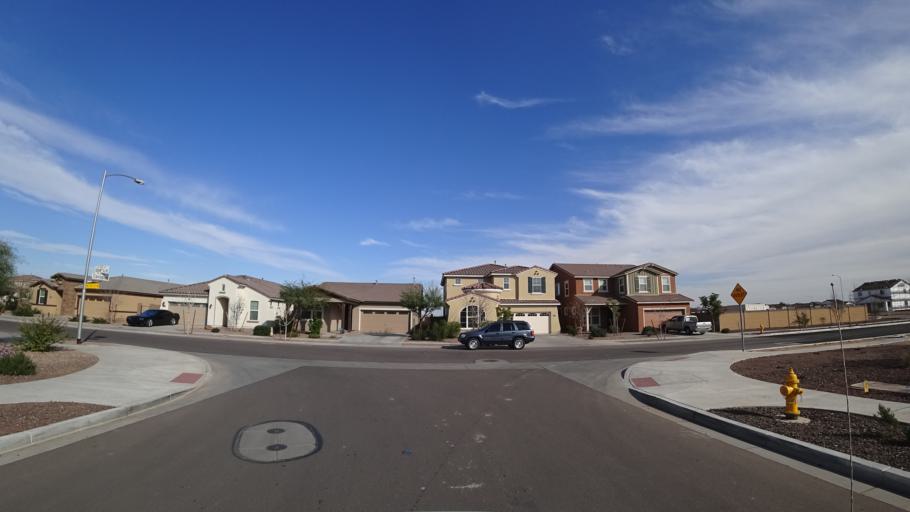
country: US
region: Arizona
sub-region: Maricopa County
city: Tolleson
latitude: 33.4309
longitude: -112.2851
